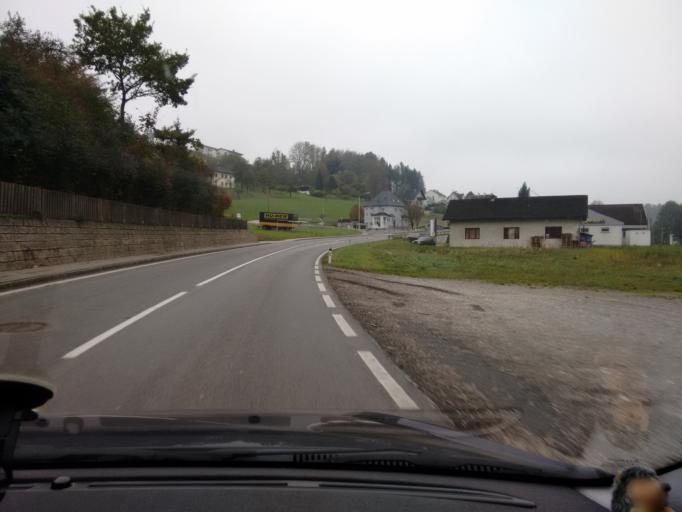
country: AT
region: Upper Austria
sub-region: Politischer Bezirk Kirchdorf an der Krems
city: Kremsmunster
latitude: 48.0505
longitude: 14.1363
